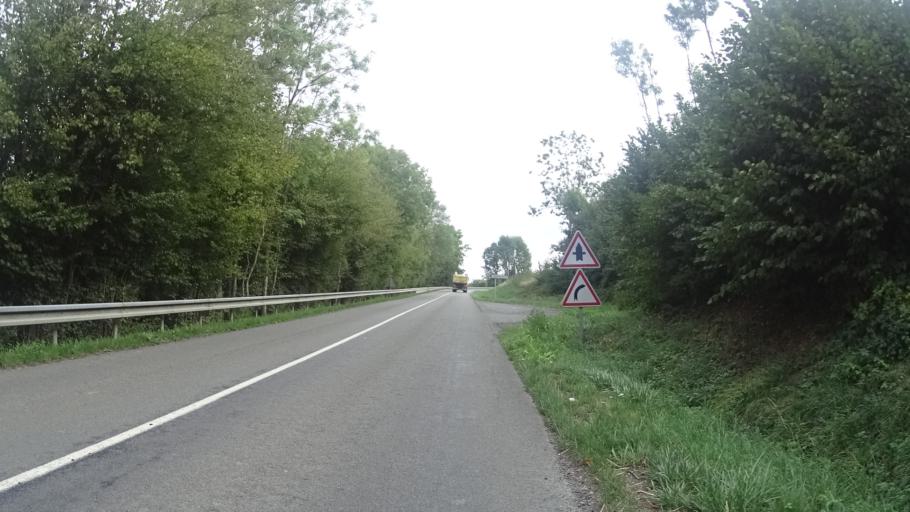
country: FR
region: Picardie
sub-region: Departement de l'Aisne
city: Guise
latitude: 49.9173
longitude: 3.5760
